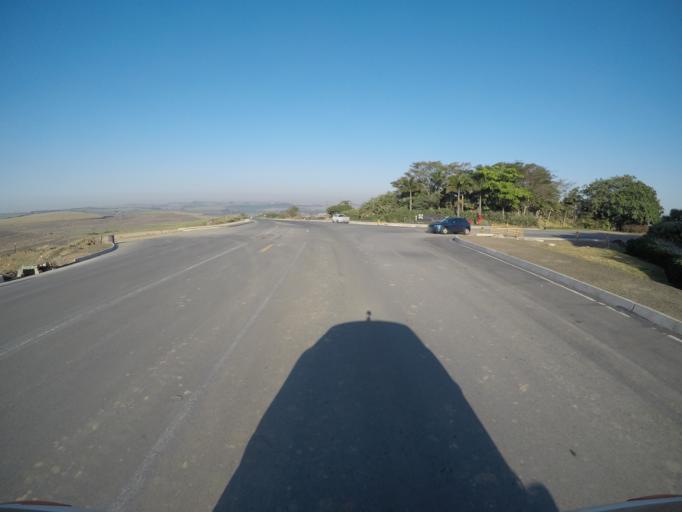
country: ZA
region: KwaZulu-Natal
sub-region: iLembe District Municipality
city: Stanger
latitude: -29.4284
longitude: 31.2575
